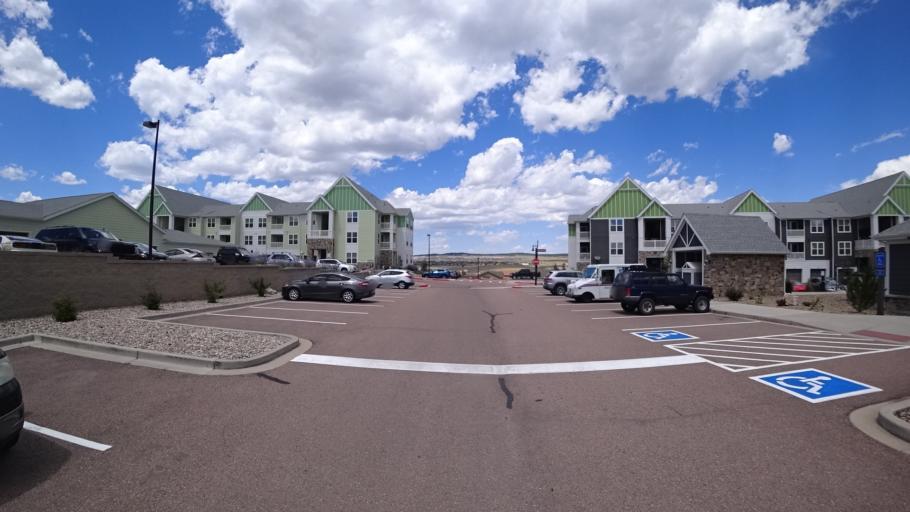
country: US
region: Colorado
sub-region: El Paso County
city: Black Forest
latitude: 38.9433
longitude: -104.7114
